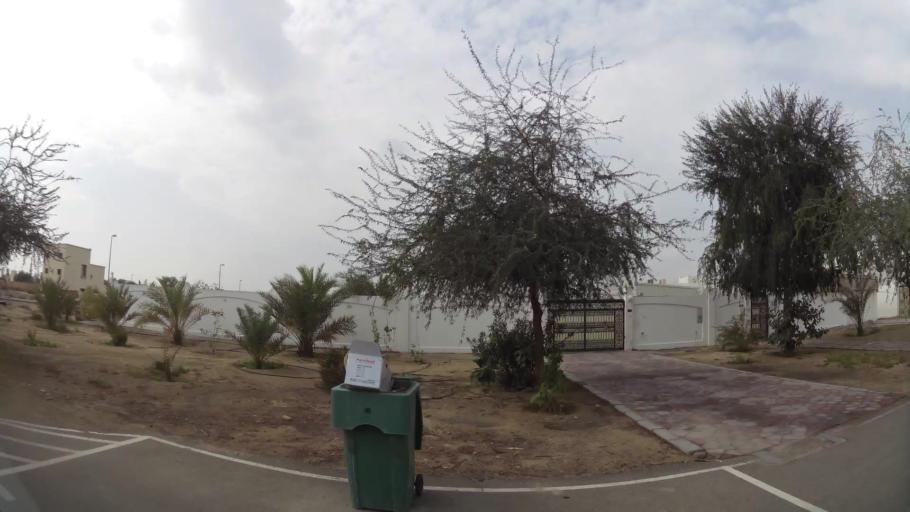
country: AE
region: Abu Dhabi
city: Abu Dhabi
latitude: 24.6370
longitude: 54.7200
